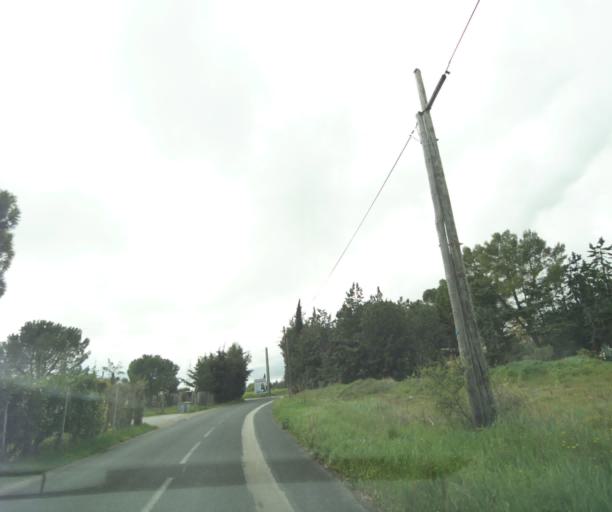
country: FR
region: Languedoc-Roussillon
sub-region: Departement de l'Herault
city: Fabregues
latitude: 43.5539
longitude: 3.7595
